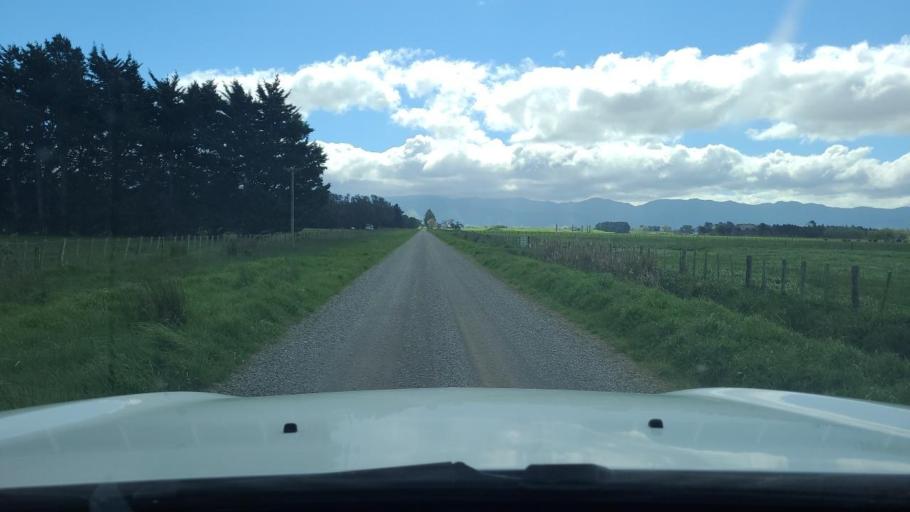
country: NZ
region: Wellington
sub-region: South Wairarapa District
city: Waipawa
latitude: -41.2436
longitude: 175.3077
